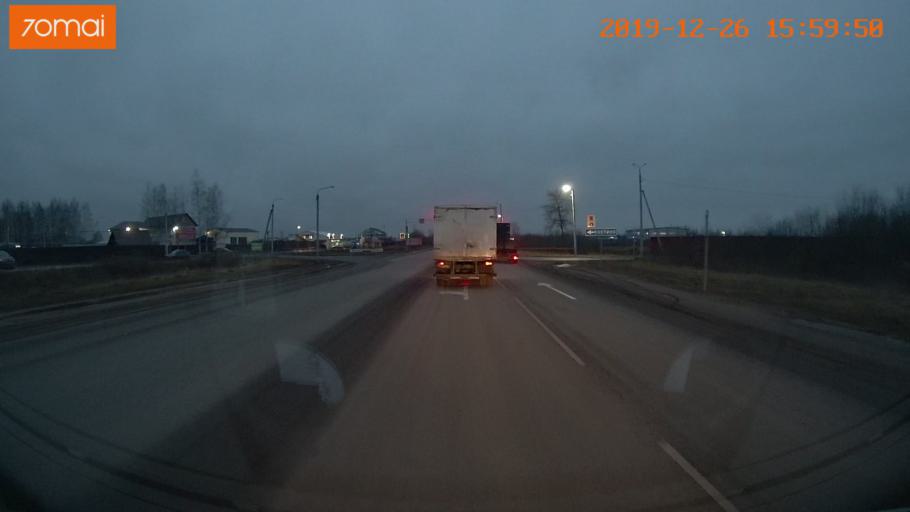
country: RU
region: Jaroslavl
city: Rybinsk
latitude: 58.0290
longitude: 38.8042
